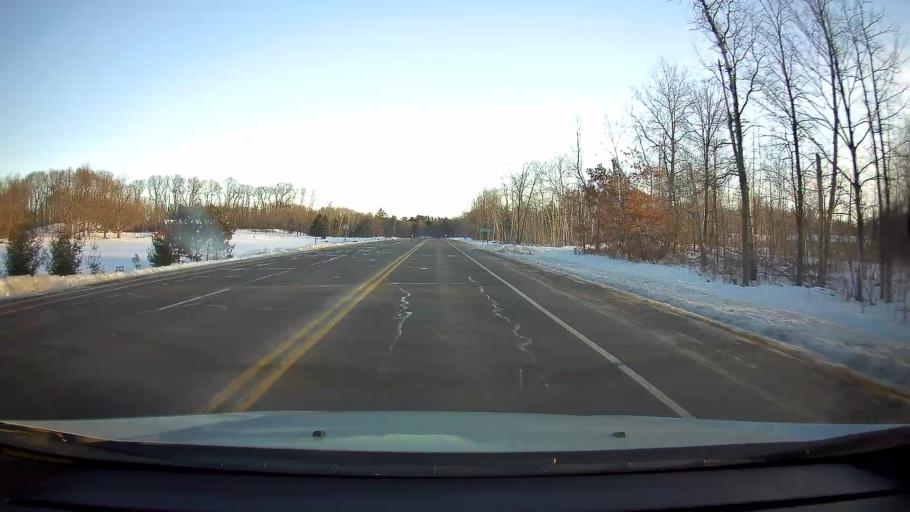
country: US
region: Wisconsin
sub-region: Barron County
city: Turtle Lake
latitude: 45.4506
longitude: -92.1067
